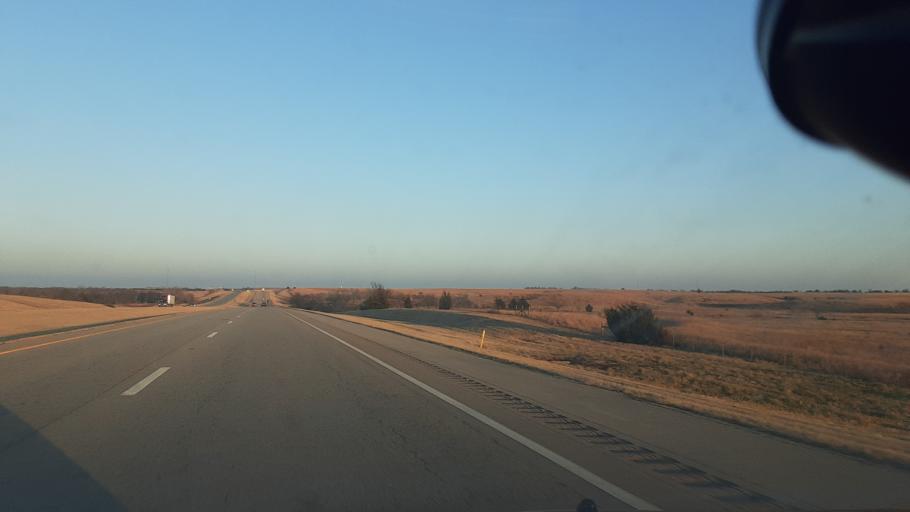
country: US
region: Oklahoma
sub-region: Noble County
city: Perry
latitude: 36.3980
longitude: -97.3695
